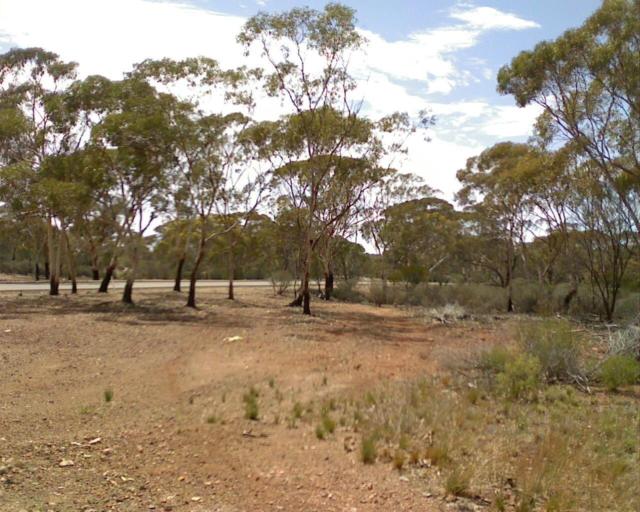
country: AU
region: Western Australia
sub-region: Kalgoorlie/Boulder
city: Stoneville
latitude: -31.2029
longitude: 121.6572
